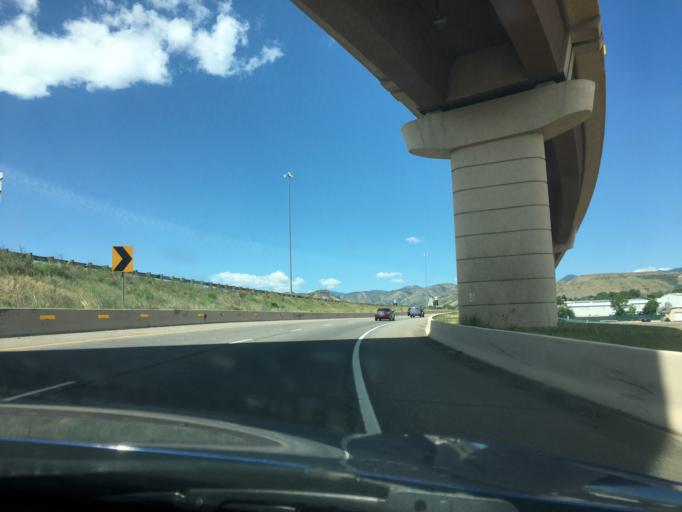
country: US
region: Colorado
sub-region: Jefferson County
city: Applewood
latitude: 39.7755
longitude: -105.1449
